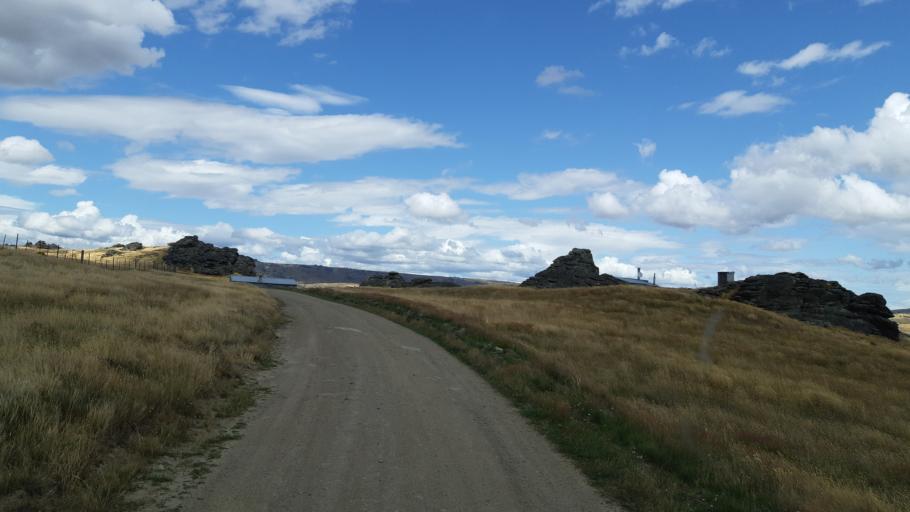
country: NZ
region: Otago
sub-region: Queenstown-Lakes District
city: Wanaka
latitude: -45.2959
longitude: 169.7444
